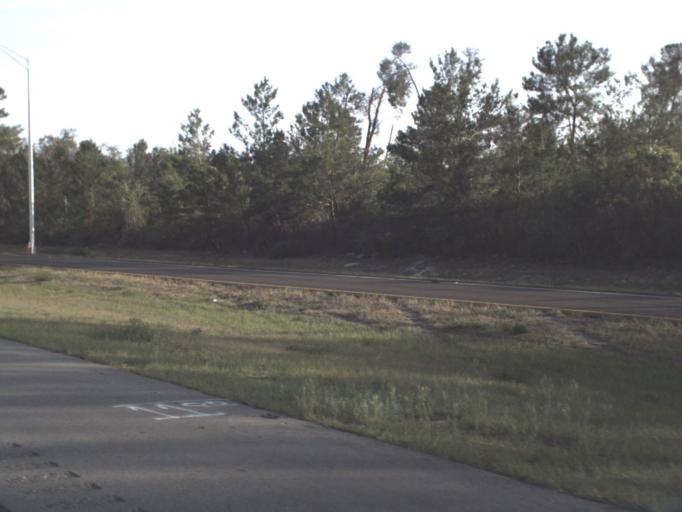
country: US
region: Florida
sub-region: Brevard County
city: Mims
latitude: 28.6632
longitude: -80.8686
